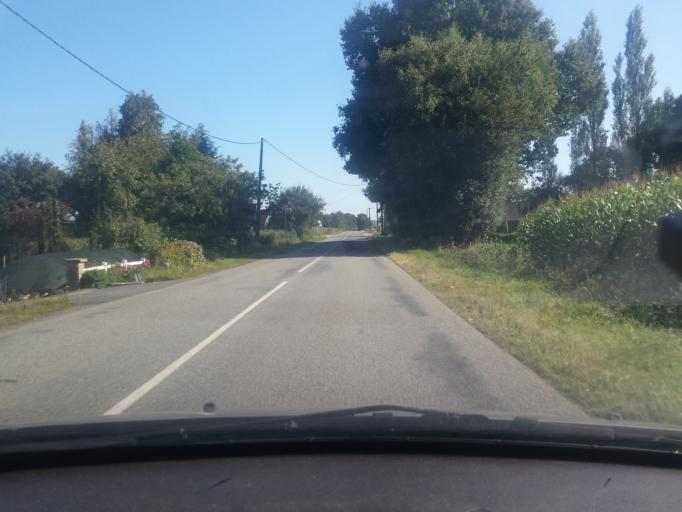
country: FR
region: Brittany
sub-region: Departement du Morbihan
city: Cleguerec
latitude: 48.1155
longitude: -3.1211
